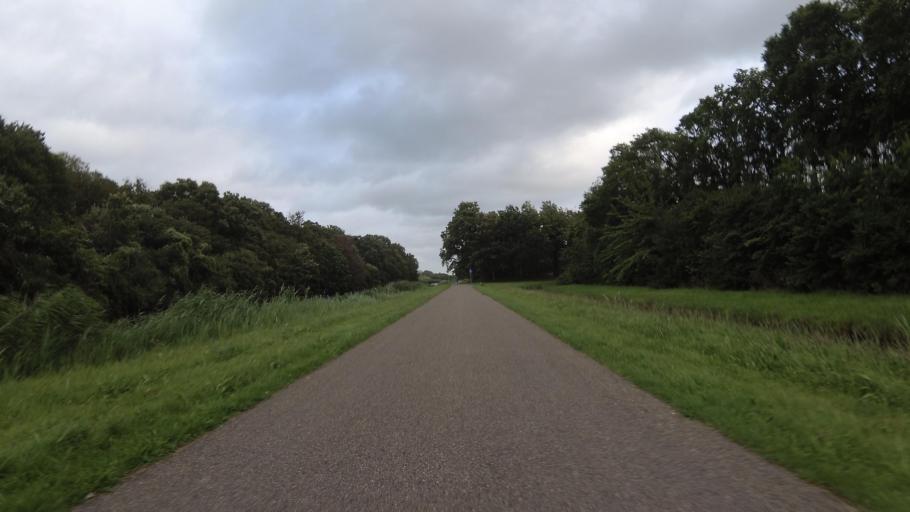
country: NL
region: North Holland
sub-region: Gemeente Den Helder
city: Den Helder
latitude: 52.9541
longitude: 4.7470
